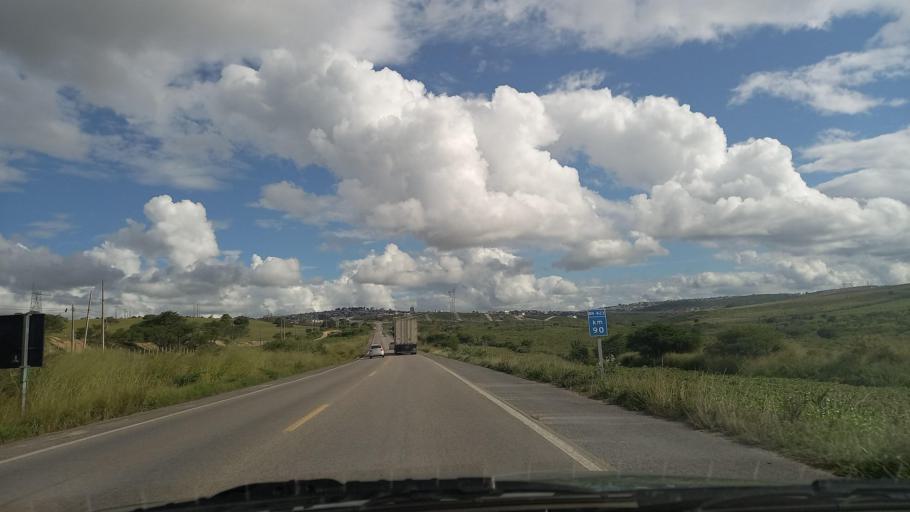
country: BR
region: Pernambuco
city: Garanhuns
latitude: -8.8444
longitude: -36.4592
